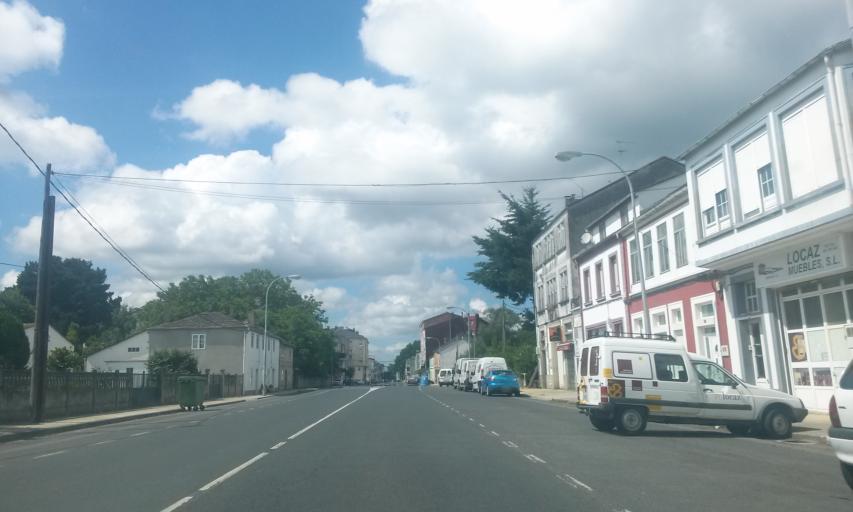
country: ES
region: Galicia
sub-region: Provincia de Lugo
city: Rabade
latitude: 43.1210
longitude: -7.6203
